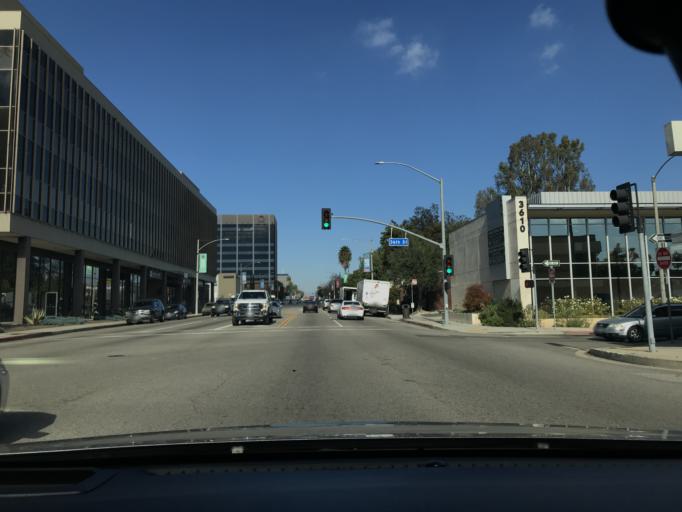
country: US
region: California
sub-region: Los Angeles County
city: Signal Hill
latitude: 33.8220
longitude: -118.1893
